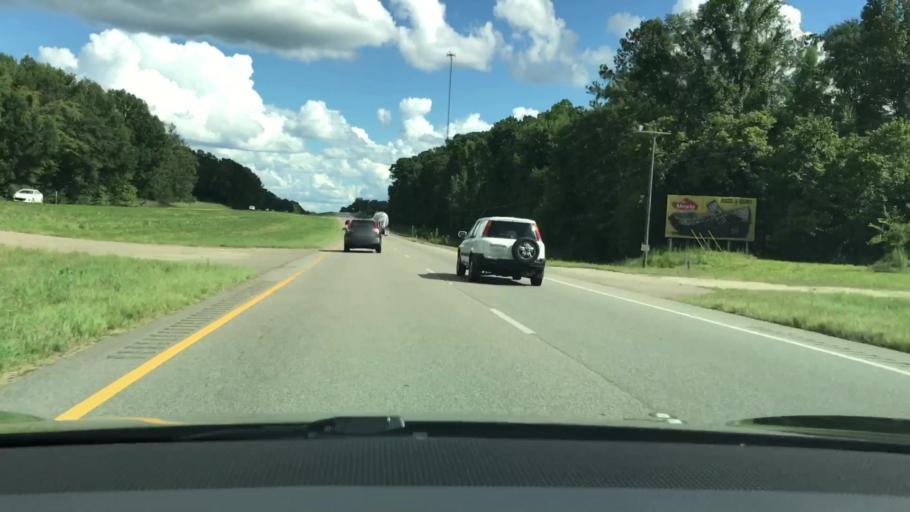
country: US
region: Alabama
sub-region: Montgomery County
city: Pike Road
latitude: 32.1324
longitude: -86.0860
